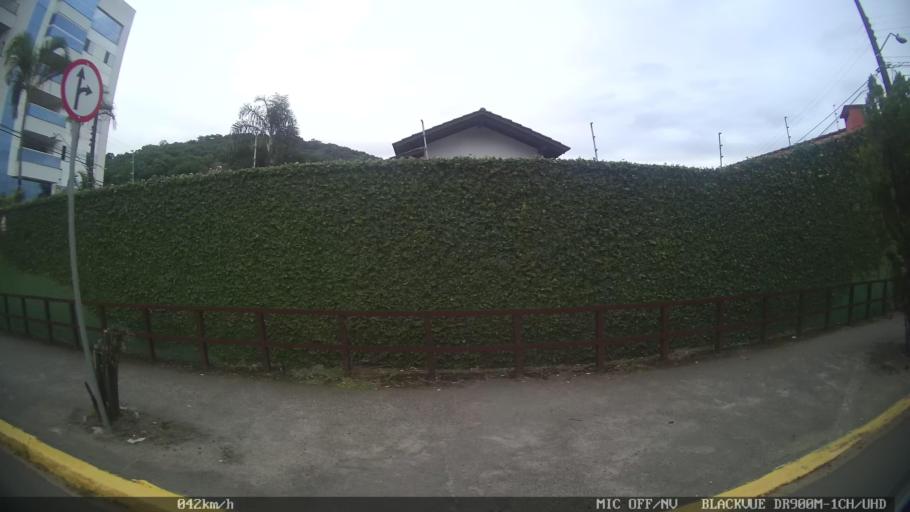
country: BR
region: Santa Catarina
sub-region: Joinville
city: Joinville
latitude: -26.2853
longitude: -48.8615
